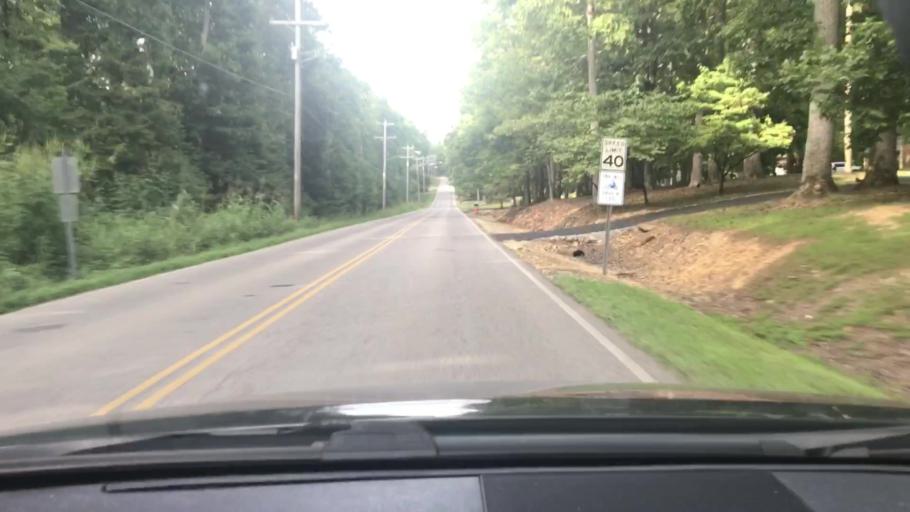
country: US
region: Tennessee
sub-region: Dickson County
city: White Bluff
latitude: 36.0758
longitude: -87.2215
